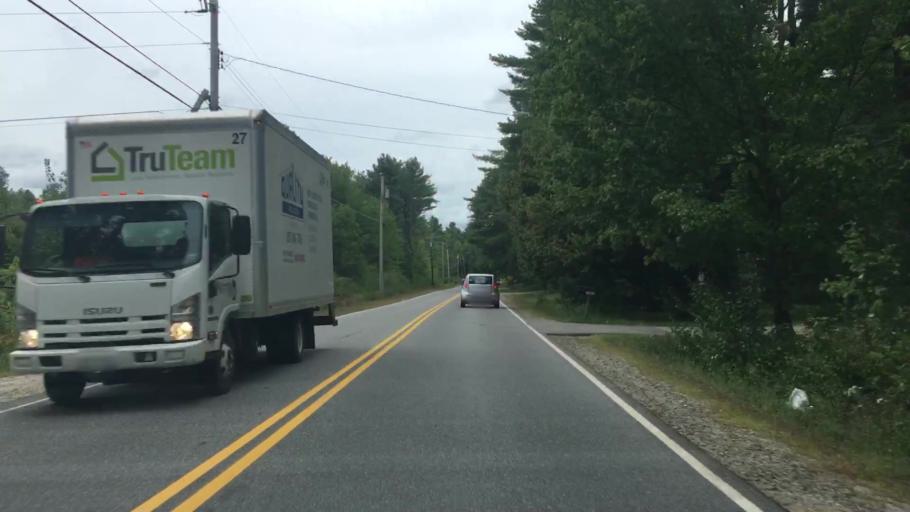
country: US
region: Maine
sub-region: Cumberland County
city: Cumberland Center
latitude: 43.8697
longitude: -70.2298
